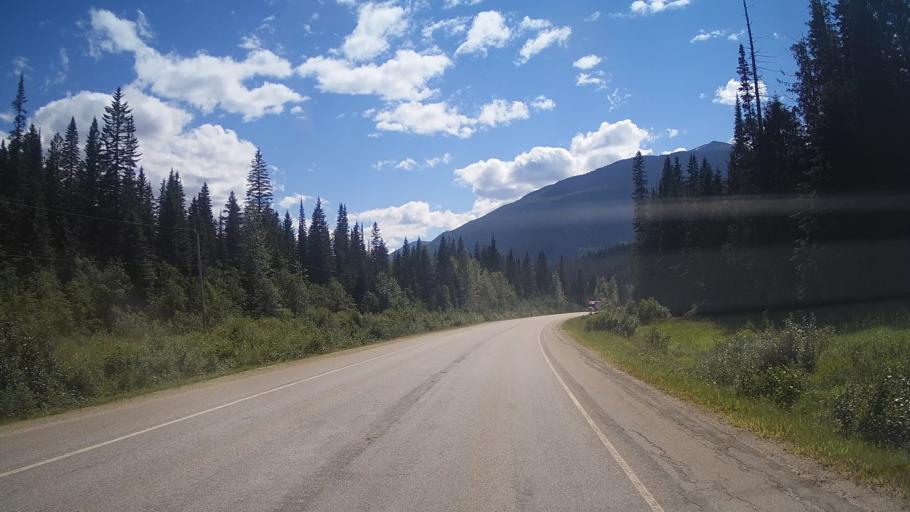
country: CA
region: Alberta
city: Jasper Park Lodge
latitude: 52.5691
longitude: -119.1014
